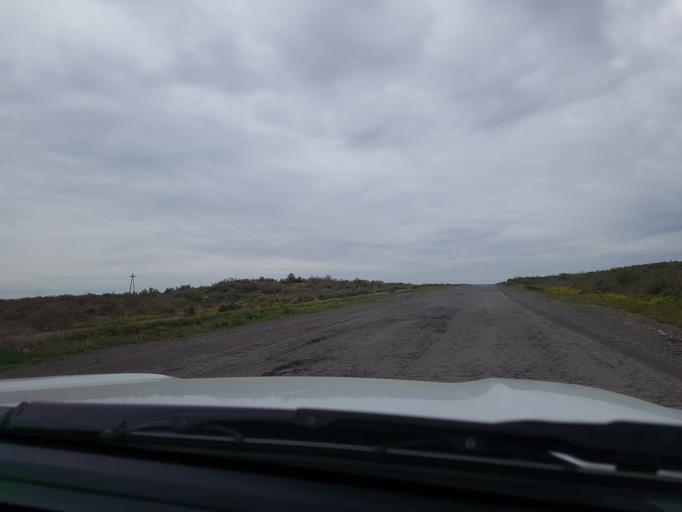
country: TM
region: Mary
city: Bayramaly
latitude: 37.9142
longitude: 62.6218
